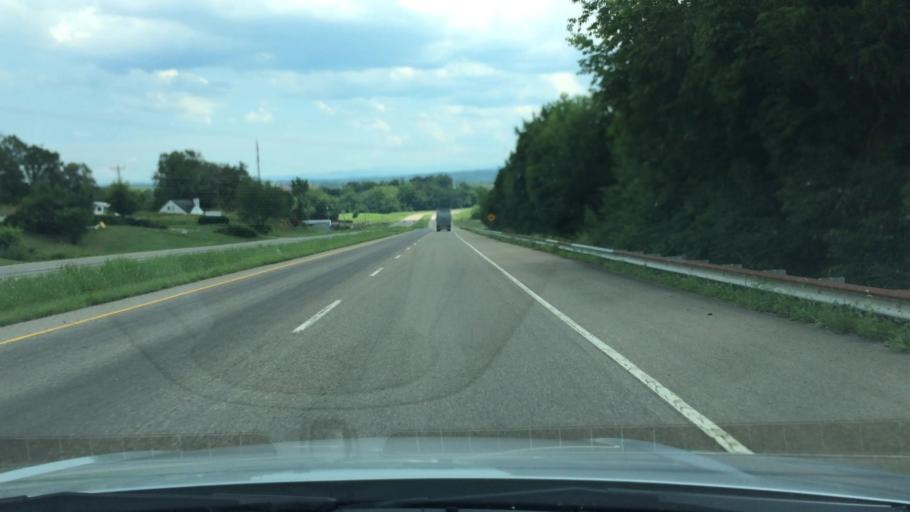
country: US
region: Tennessee
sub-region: Jefferson County
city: White Pine
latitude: 36.1651
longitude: -83.2169
